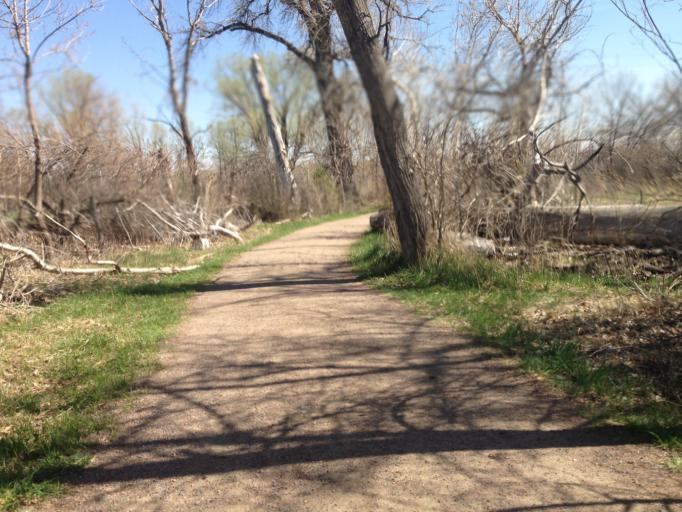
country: US
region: Colorado
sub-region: Boulder County
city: Boulder
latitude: 39.9870
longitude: -105.2199
